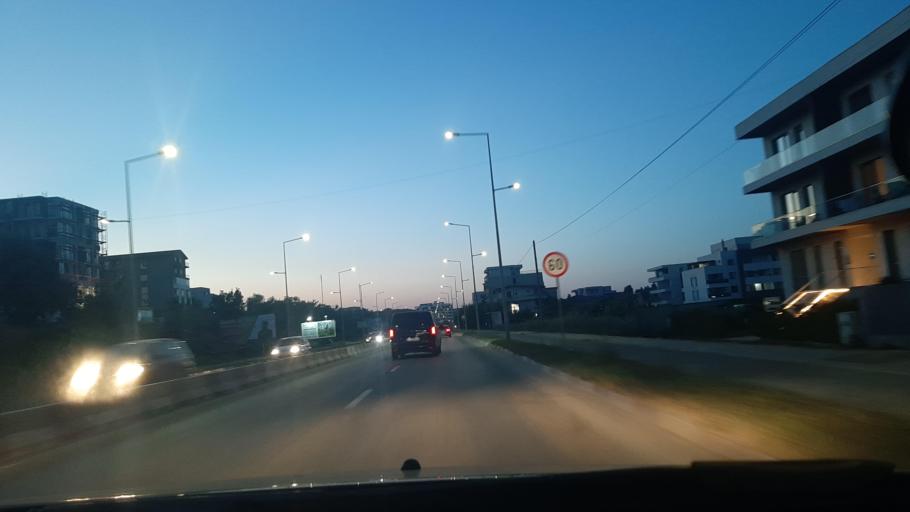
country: RO
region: Constanta
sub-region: Comuna Navodari
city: Navodari
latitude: 44.2954
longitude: 28.6194
